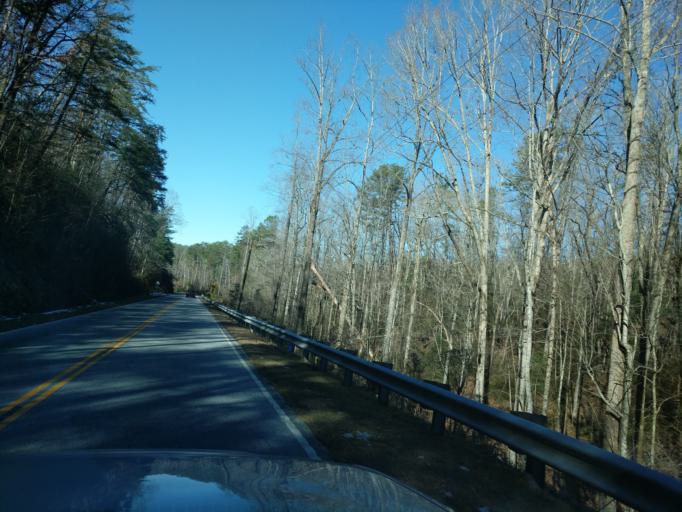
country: US
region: South Carolina
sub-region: Oconee County
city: Westminster
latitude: 34.7541
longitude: -83.2374
